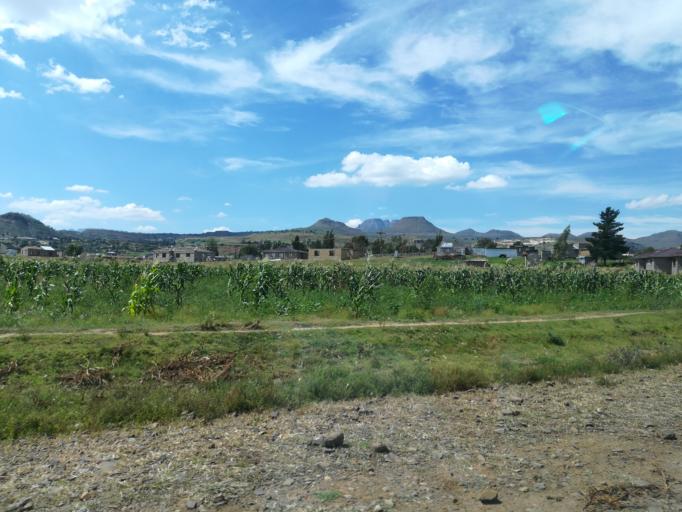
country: LS
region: Mohale's Hoek District
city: Mohale's Hoek
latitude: -30.1077
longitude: 27.4675
